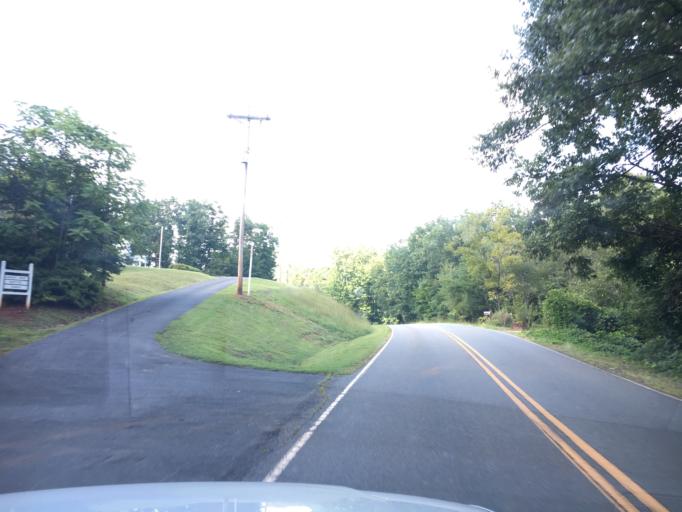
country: US
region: North Carolina
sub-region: Rutherford County
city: Lake Lure
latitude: 35.4077
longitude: -82.1722
